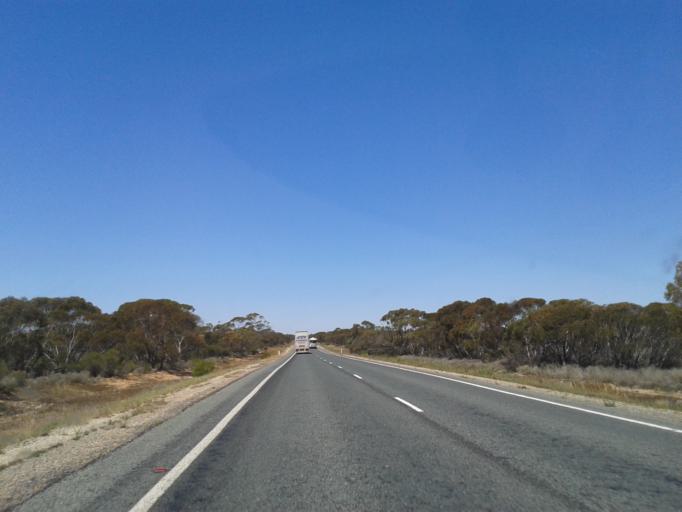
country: AU
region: New South Wales
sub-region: Wentworth
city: Gol Gol
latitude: -34.4921
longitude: 142.5692
